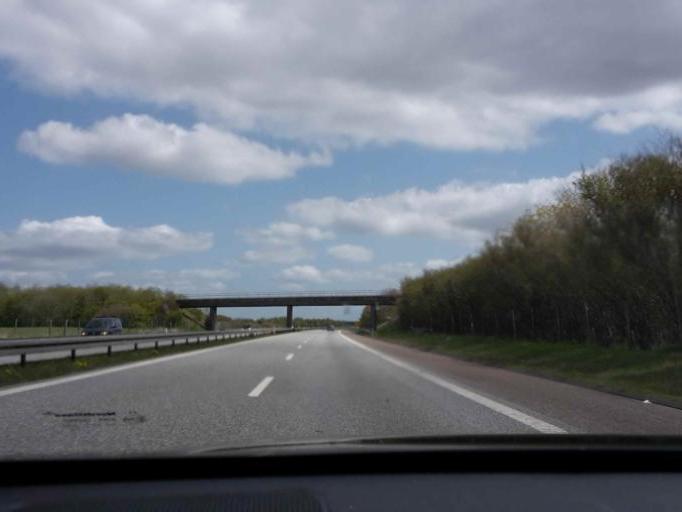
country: DK
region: South Denmark
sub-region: Esbjerg Kommune
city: Bramming
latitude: 55.5144
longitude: 8.7770
